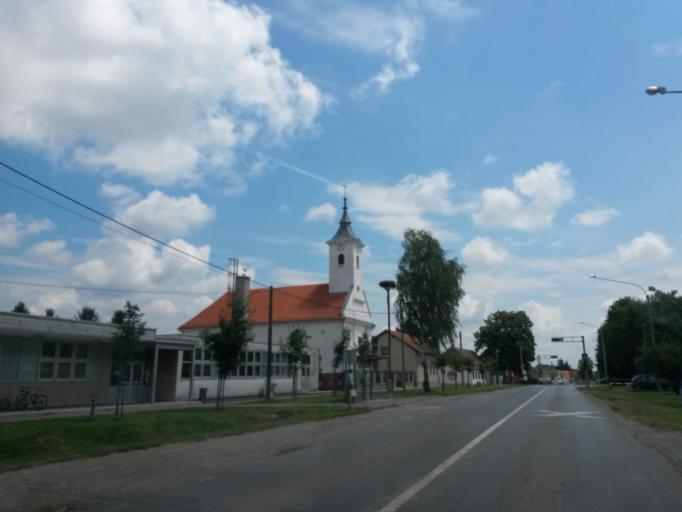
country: HR
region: Osjecko-Baranjska
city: Sarvas
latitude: 45.5246
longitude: 18.8411
